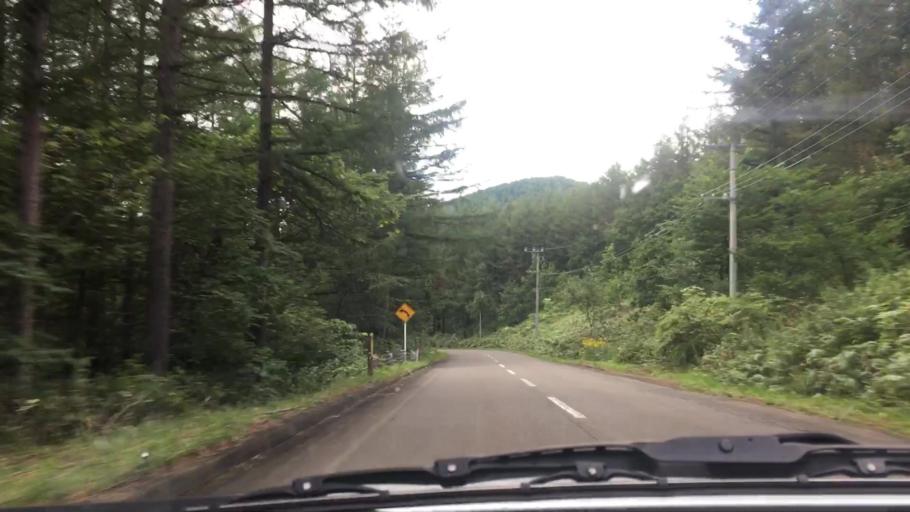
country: JP
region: Hokkaido
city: Otofuke
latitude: 43.1543
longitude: 142.8580
